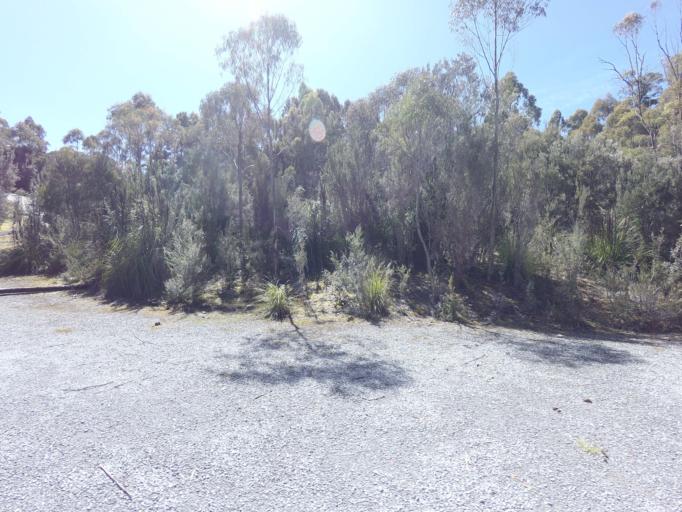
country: AU
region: Tasmania
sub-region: Huon Valley
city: Geeveston
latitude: -43.0389
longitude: 146.2991
